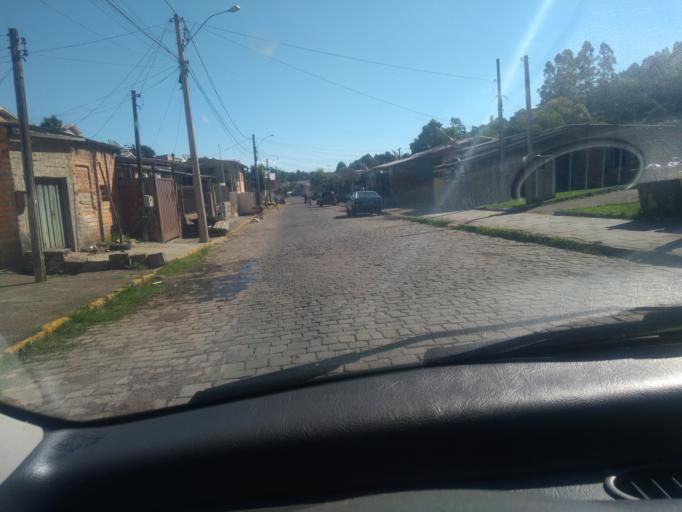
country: BR
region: Rio Grande do Sul
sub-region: Veranopolis
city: Veranopolis
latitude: -28.9373
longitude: -51.5592
